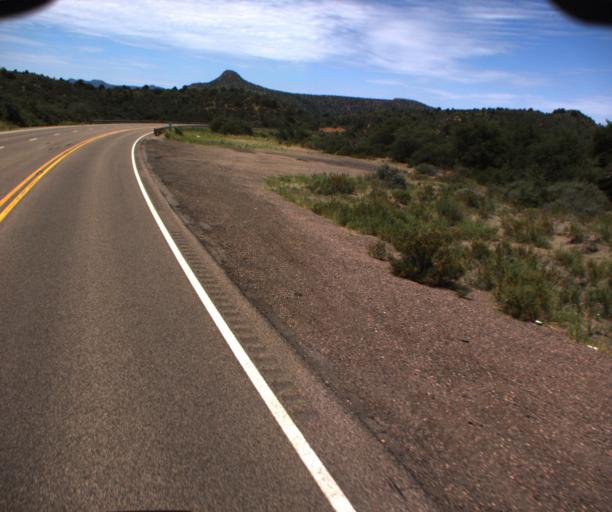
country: US
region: Arizona
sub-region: Gila County
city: San Carlos
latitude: 33.6393
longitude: -110.5771
